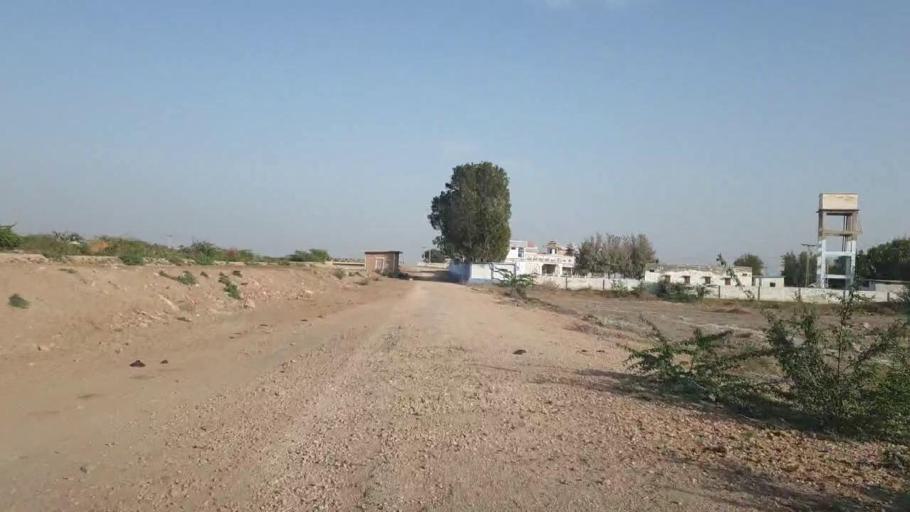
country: PK
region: Sindh
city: Dhoro Naro
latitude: 25.4844
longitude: 69.5850
